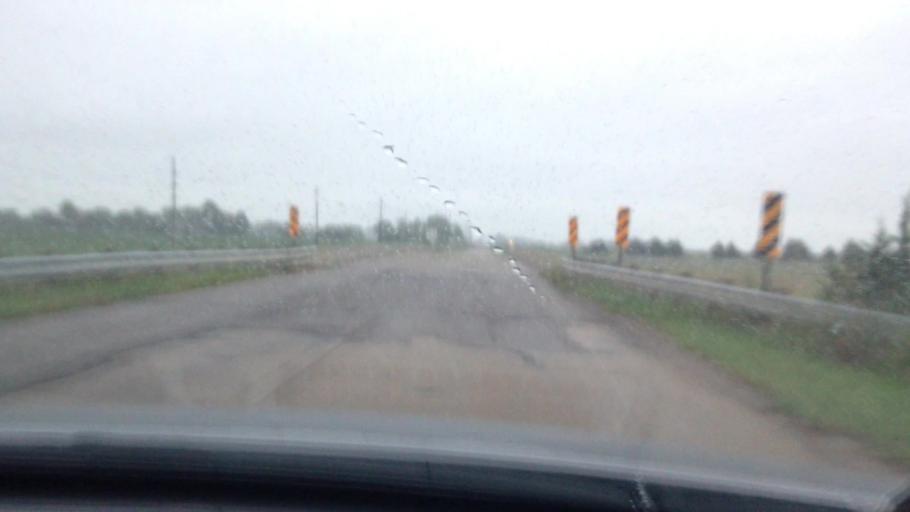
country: US
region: Kansas
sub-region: Brown County
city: Hiawatha
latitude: 39.8416
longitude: -95.5458
